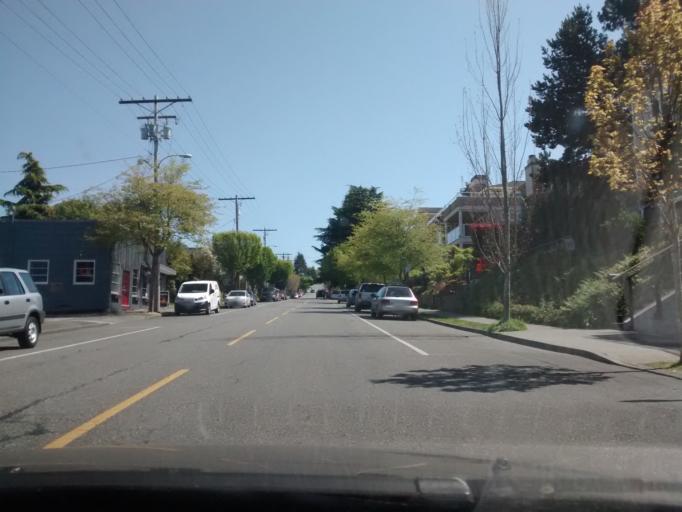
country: US
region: Washington
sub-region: Snohomish County
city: Edmonds
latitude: 47.8097
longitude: -122.3770
